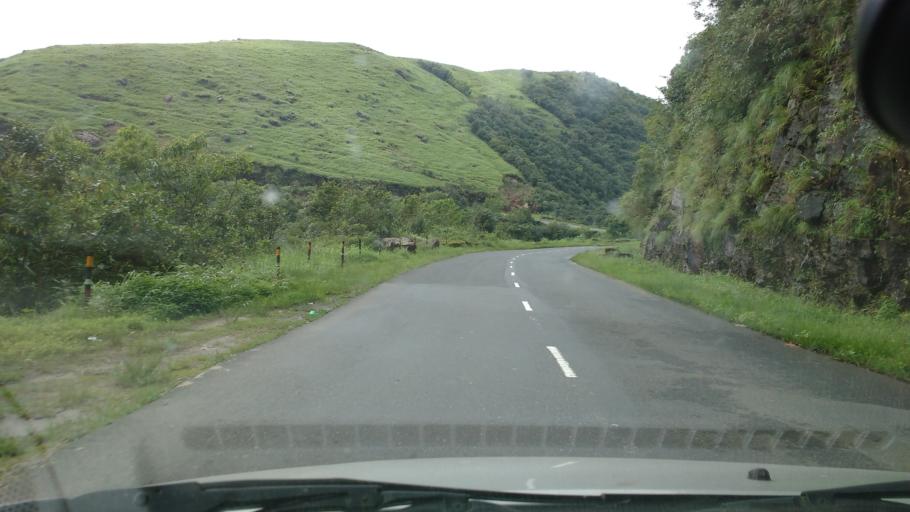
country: IN
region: Meghalaya
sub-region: East Khasi Hills
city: Shillong
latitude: 25.3865
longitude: 91.8744
